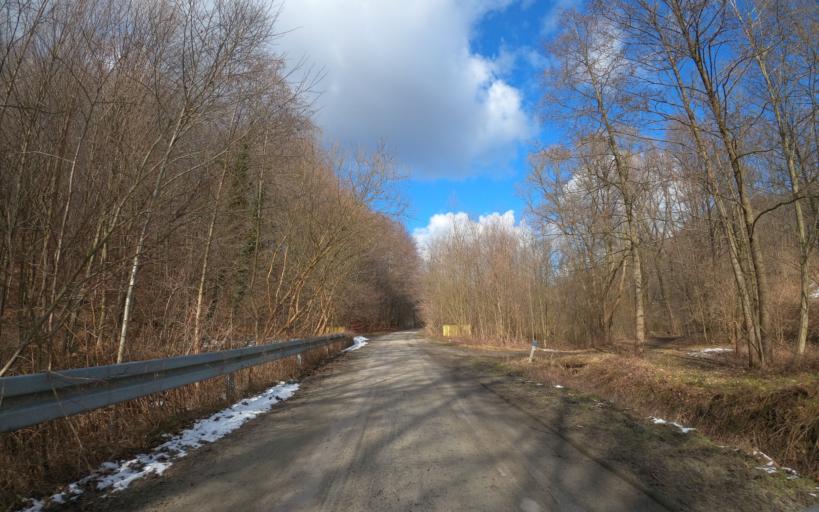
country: PL
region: Subcarpathian Voivodeship
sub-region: Powiat debicki
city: Debica
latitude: 50.0247
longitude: 21.4343
